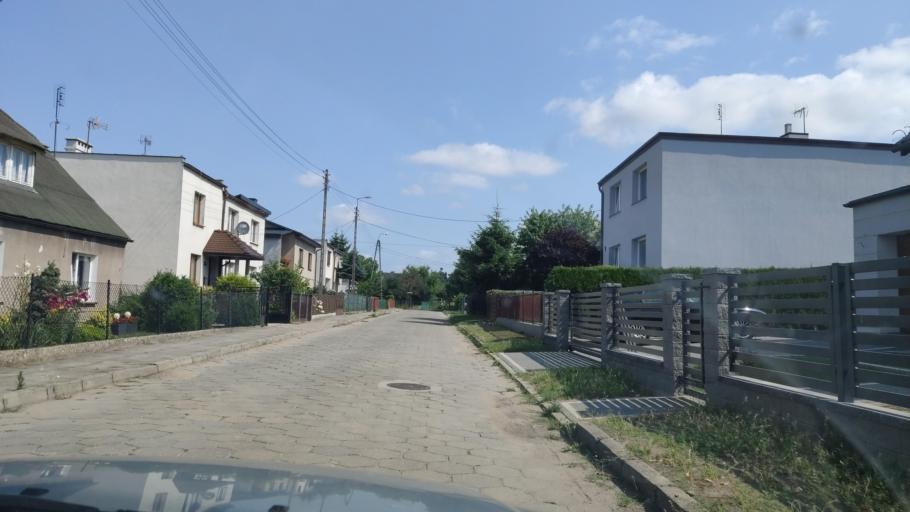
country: PL
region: Kujawsko-Pomorskie
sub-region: Powiat zninski
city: Znin
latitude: 52.8499
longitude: 17.7513
